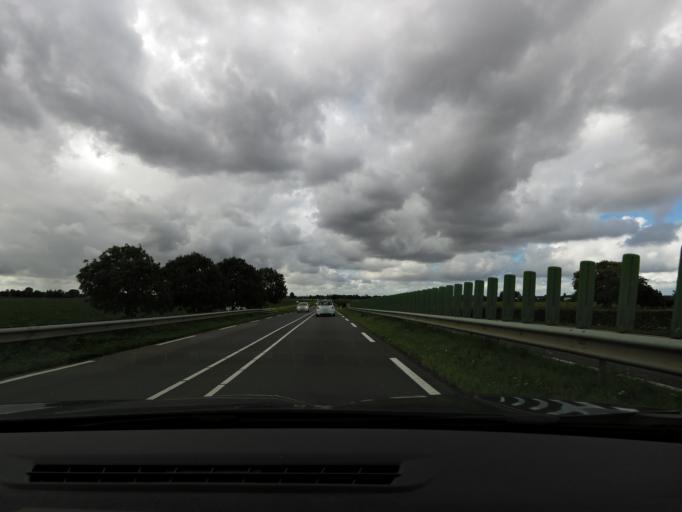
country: NL
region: South Holland
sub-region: Gemeente Binnenmaas
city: Heinenoord
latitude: 51.8223
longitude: 4.4573
